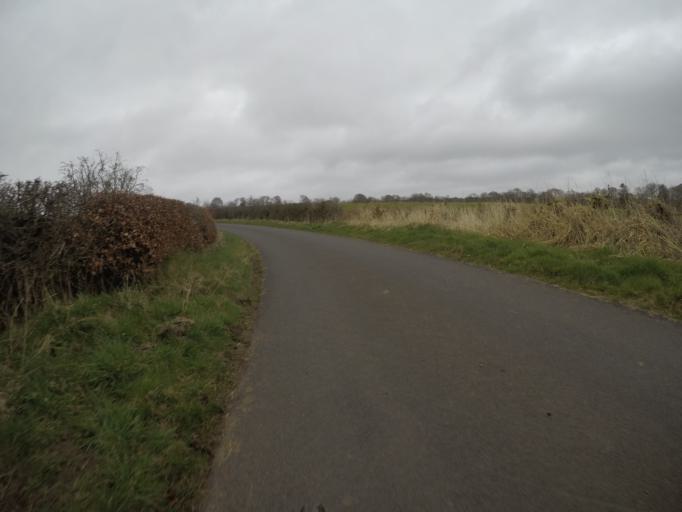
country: GB
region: Scotland
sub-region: East Ayrshire
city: Newmilns
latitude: 55.6195
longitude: -4.3537
